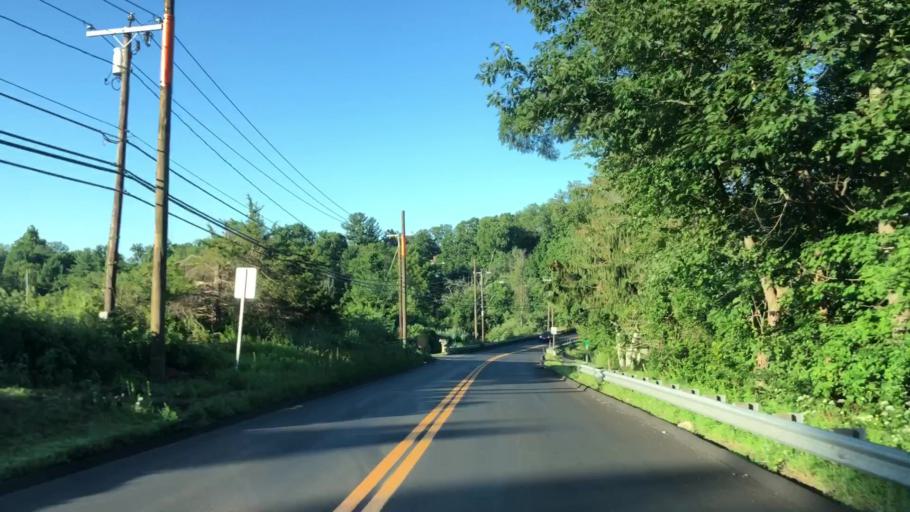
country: US
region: Massachusetts
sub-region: Hampshire County
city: Southampton
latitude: 42.2319
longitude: -72.7277
